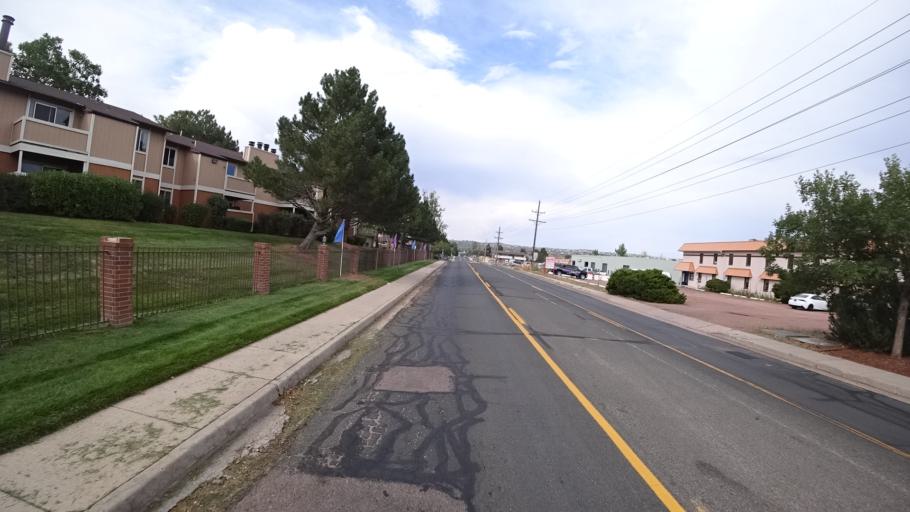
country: US
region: Colorado
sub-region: El Paso County
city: Cimarron Hills
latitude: 38.8802
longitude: -104.7610
